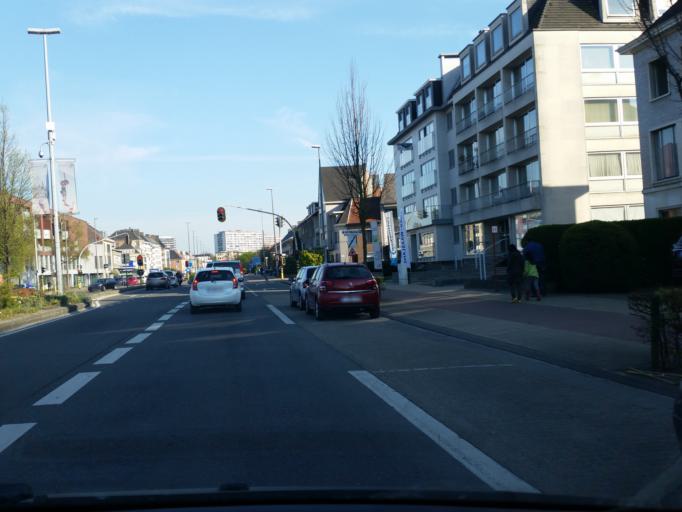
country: BE
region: Flanders
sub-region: Provincie Oost-Vlaanderen
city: Sint-Niklaas
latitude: 51.1605
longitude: 4.1474
